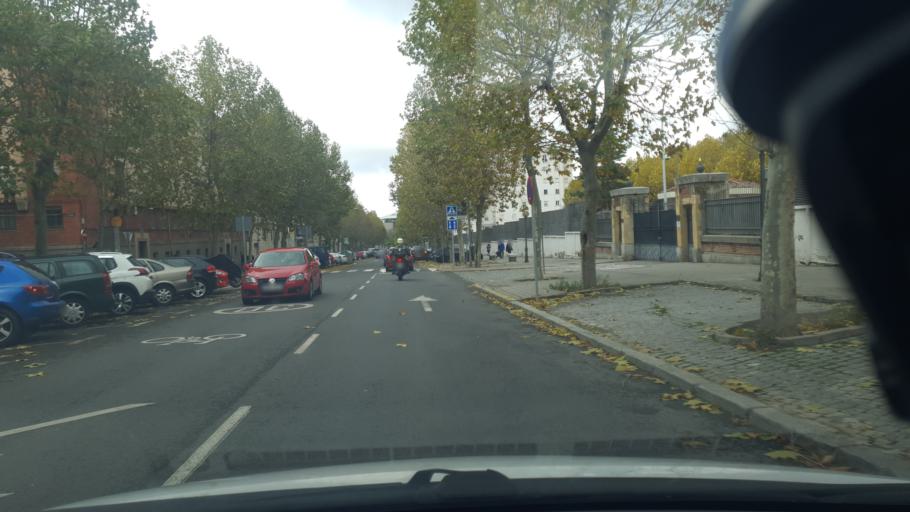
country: ES
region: Castille and Leon
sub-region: Provincia de Segovia
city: Segovia
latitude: 40.9392
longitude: -4.1121
